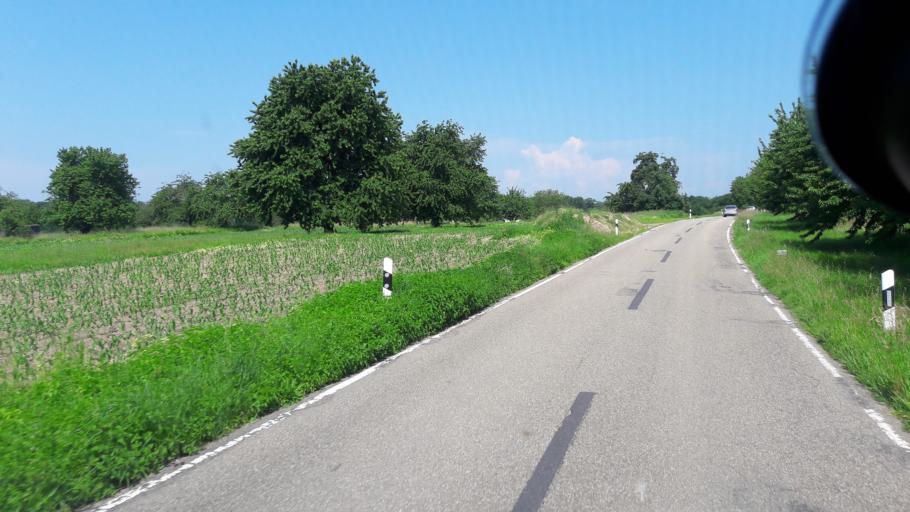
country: DE
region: Baden-Wuerttemberg
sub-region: Karlsruhe Region
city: Kuppenheim
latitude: 48.8497
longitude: 8.2486
